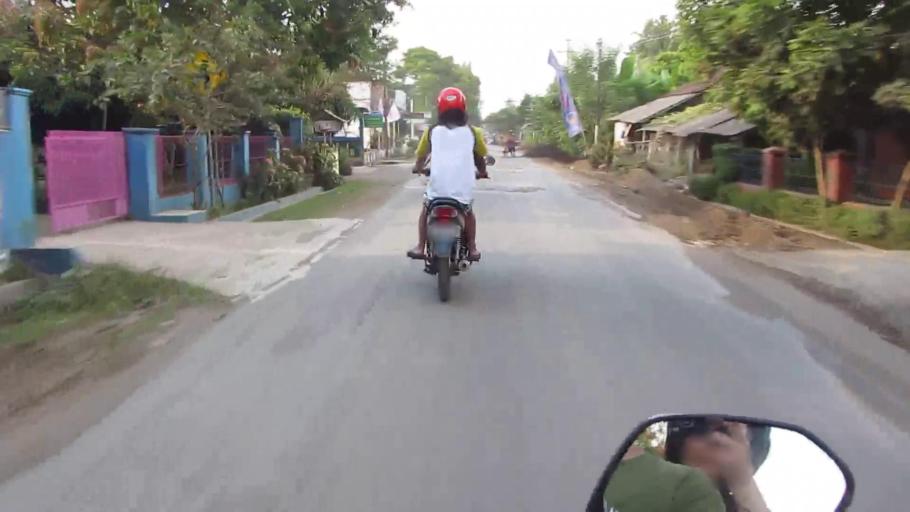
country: ID
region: West Java
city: Balengbeng
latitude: -7.7087
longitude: 108.4912
